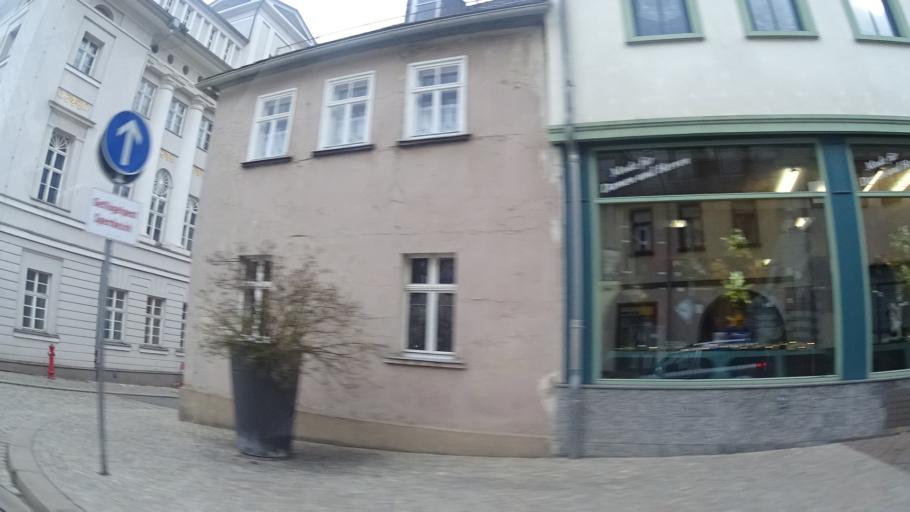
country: DE
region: Thuringia
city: Zeulenroda
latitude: 50.6484
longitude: 11.9802
